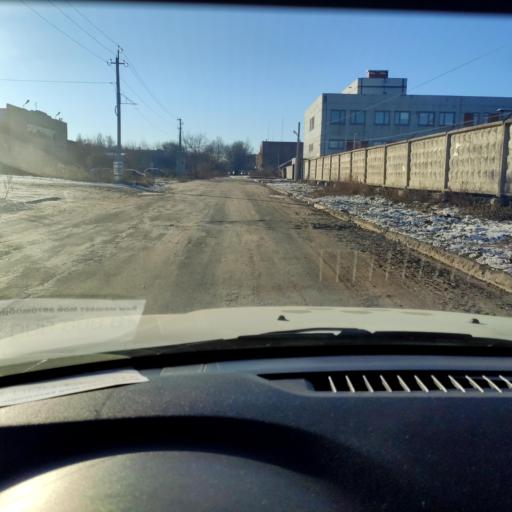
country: RU
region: Samara
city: Tol'yatti
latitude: 53.5319
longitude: 49.4359
